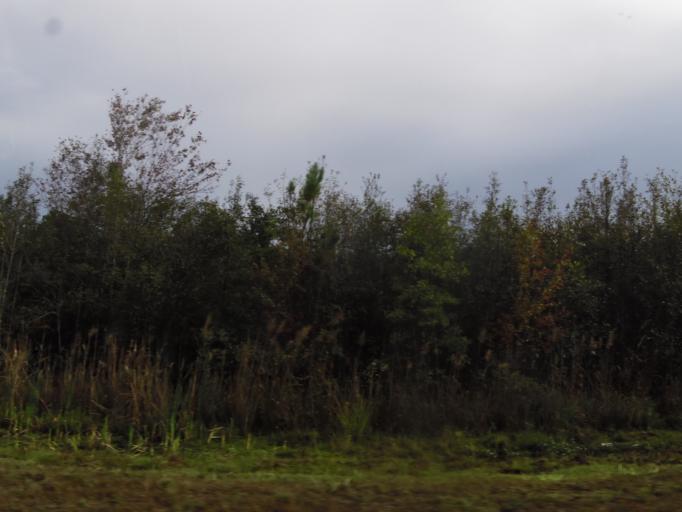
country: US
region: Georgia
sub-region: Liberty County
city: Walthourville
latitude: 31.7693
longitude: -81.6408
